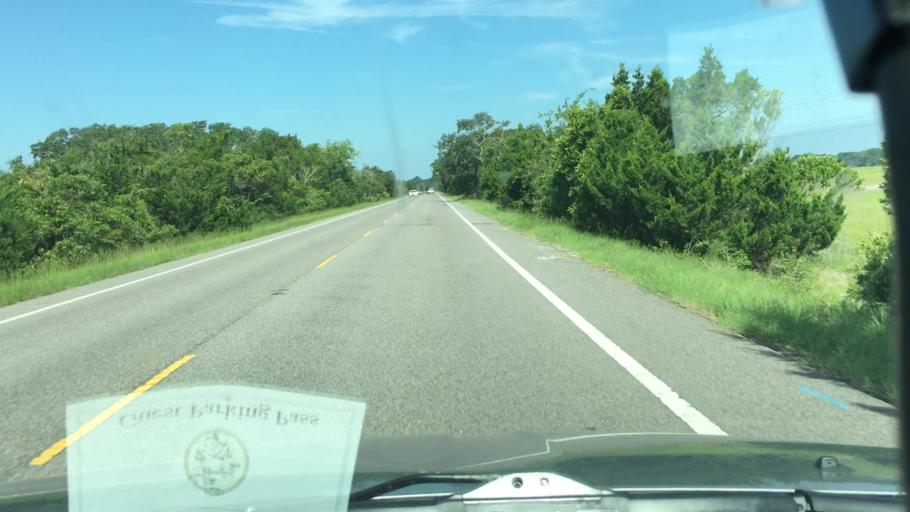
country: US
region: South Carolina
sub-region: Beaufort County
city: Beaufort
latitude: 32.4089
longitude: -80.4661
